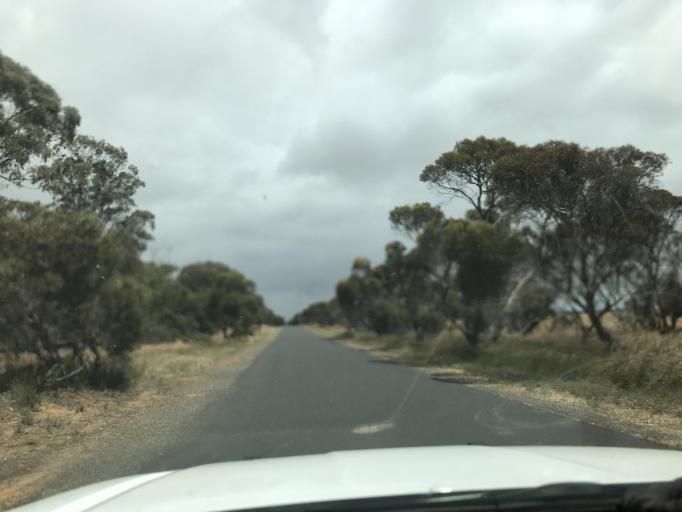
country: AU
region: South Australia
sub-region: Tatiara
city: Bordertown
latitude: -36.1212
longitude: 141.0700
